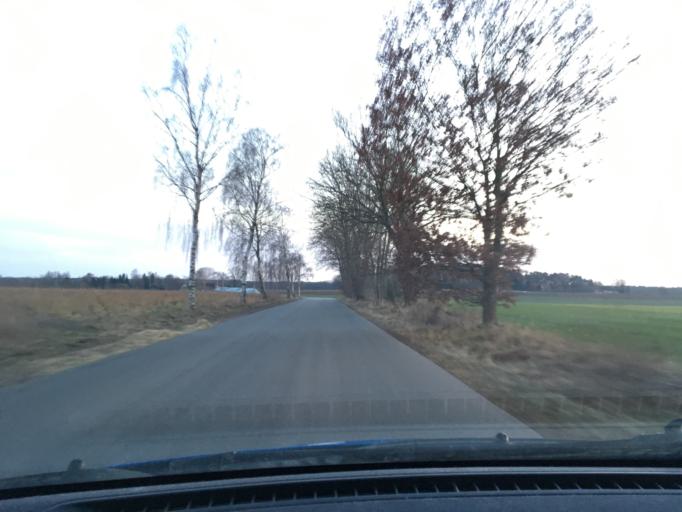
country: DE
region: Lower Saxony
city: Dahlenburg
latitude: 53.1873
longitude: 10.6974
